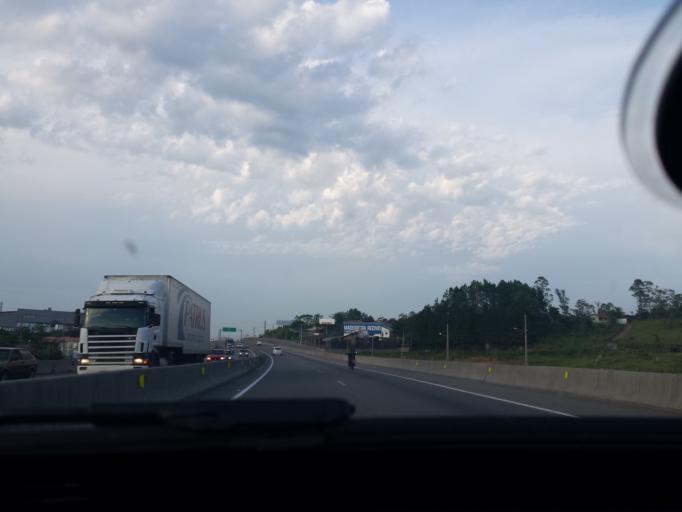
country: BR
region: Santa Catarina
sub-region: Tubarao
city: Tubarao
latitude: -28.4316
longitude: -48.9546
